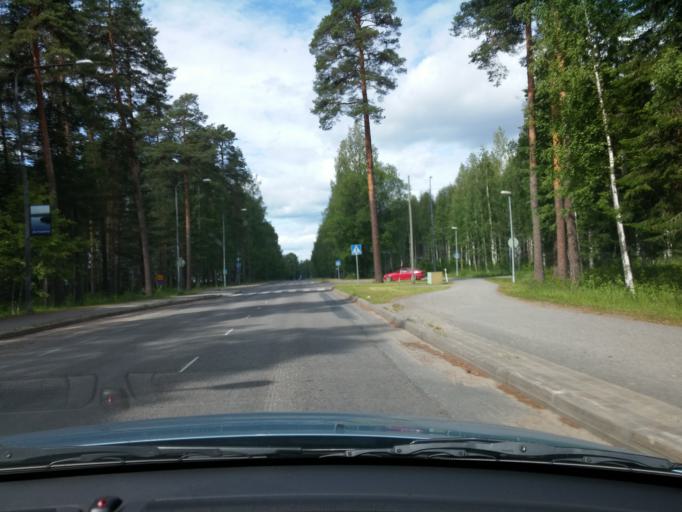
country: FI
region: Central Finland
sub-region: Saarijaervi-Viitasaari
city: Saarijaervi
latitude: 62.7062
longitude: 25.2329
